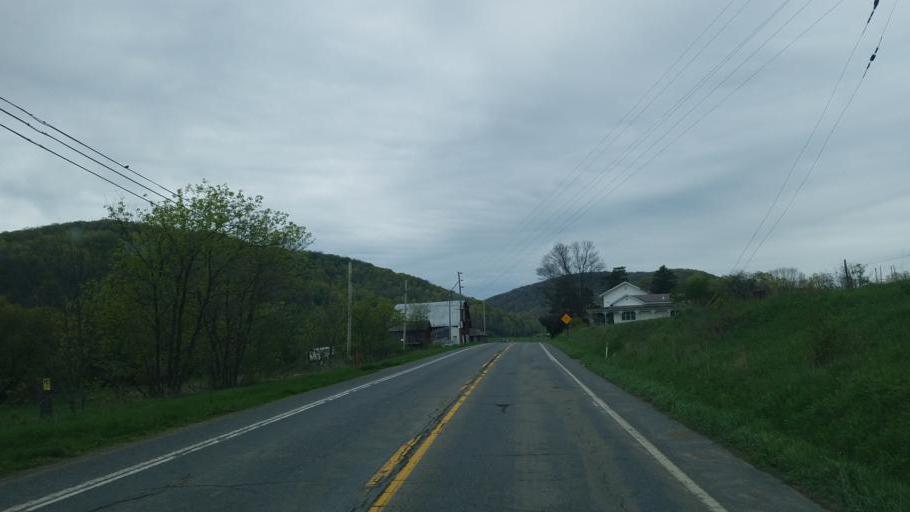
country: US
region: Pennsylvania
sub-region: Tioga County
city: Westfield
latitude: 41.9179
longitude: -77.6198
